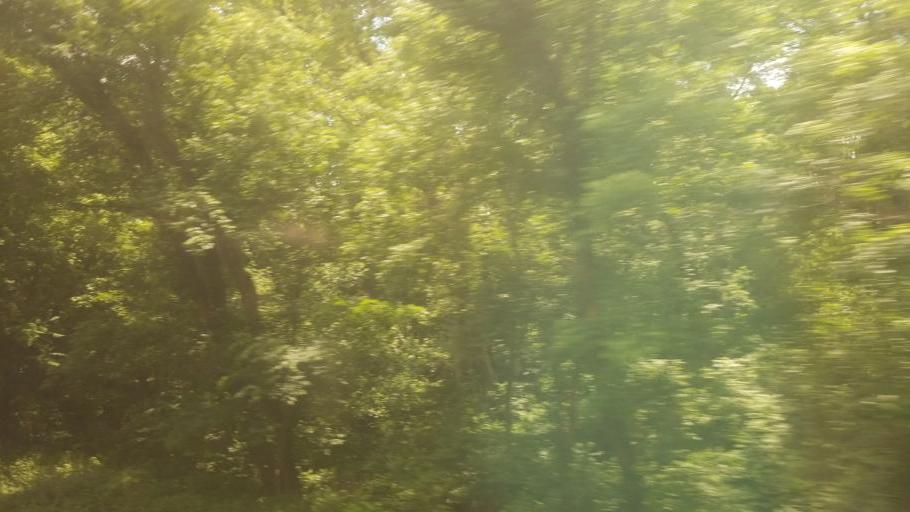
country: US
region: Maryland
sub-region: Frederick County
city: Point of Rocks
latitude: 39.3102
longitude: -77.5632
